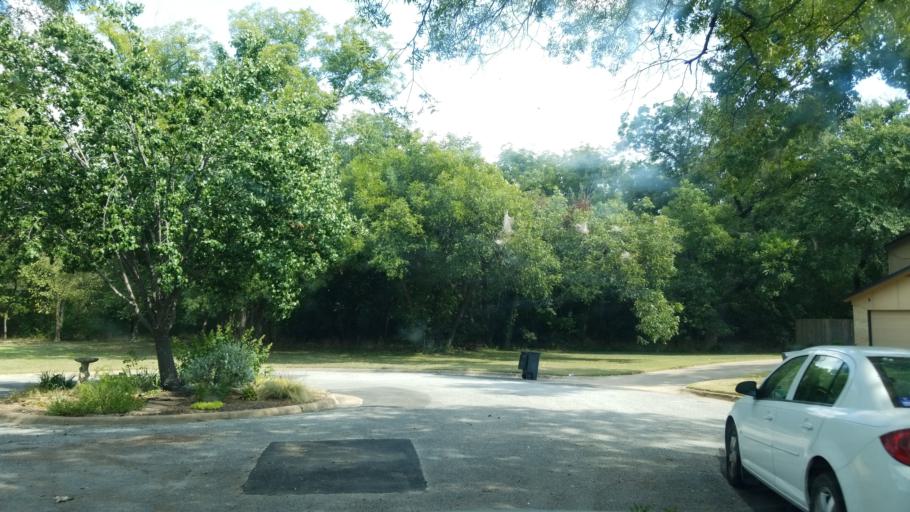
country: US
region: Texas
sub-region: Tarrant County
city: Euless
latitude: 32.8659
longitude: -97.0855
